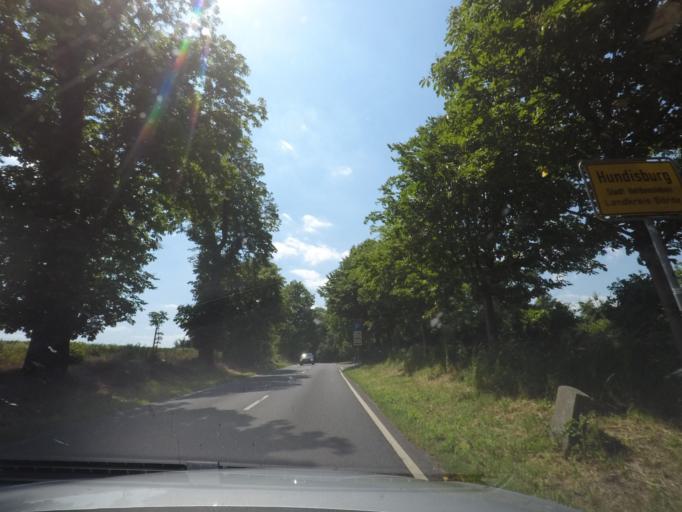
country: DE
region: Saxony-Anhalt
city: Haldensleben I
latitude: 52.2505
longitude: 11.4076
